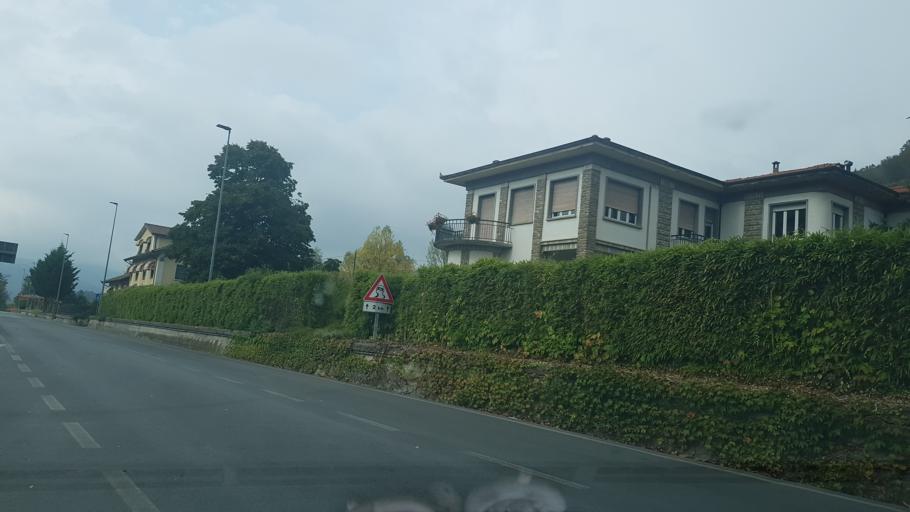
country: IT
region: Piedmont
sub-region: Provincia di Cuneo
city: Camerana
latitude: 44.4382
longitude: 8.1524
